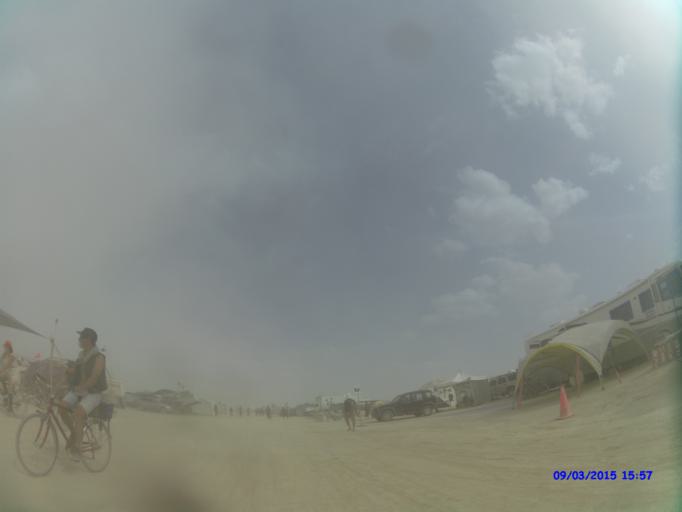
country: US
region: Nevada
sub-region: Pershing County
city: Lovelock
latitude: 40.7778
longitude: -119.2116
